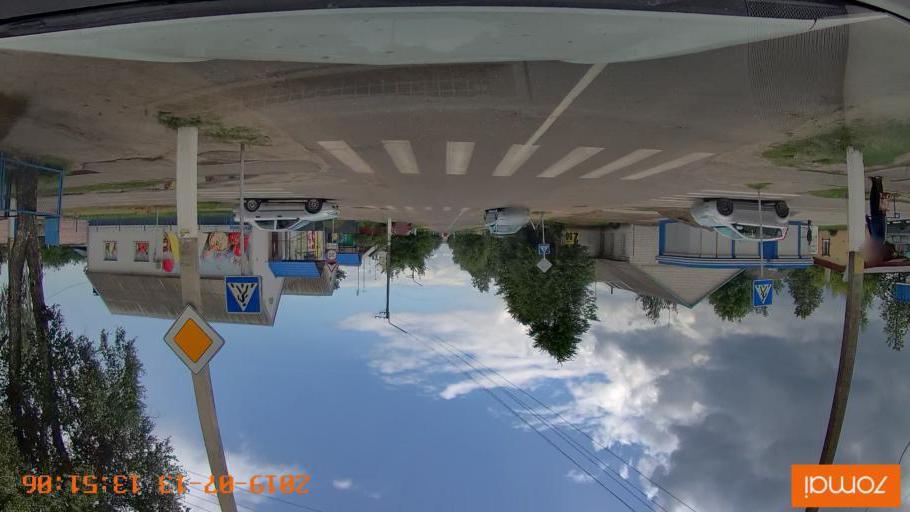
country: BY
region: Mogilev
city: Asipovichy
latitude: 53.2967
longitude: 28.6377
